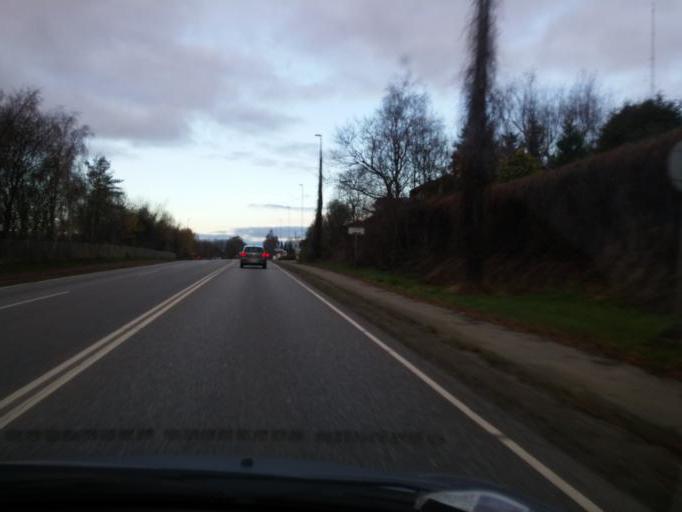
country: DK
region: South Denmark
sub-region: Vejle Kommune
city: Vejle
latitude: 55.6879
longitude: 9.5550
